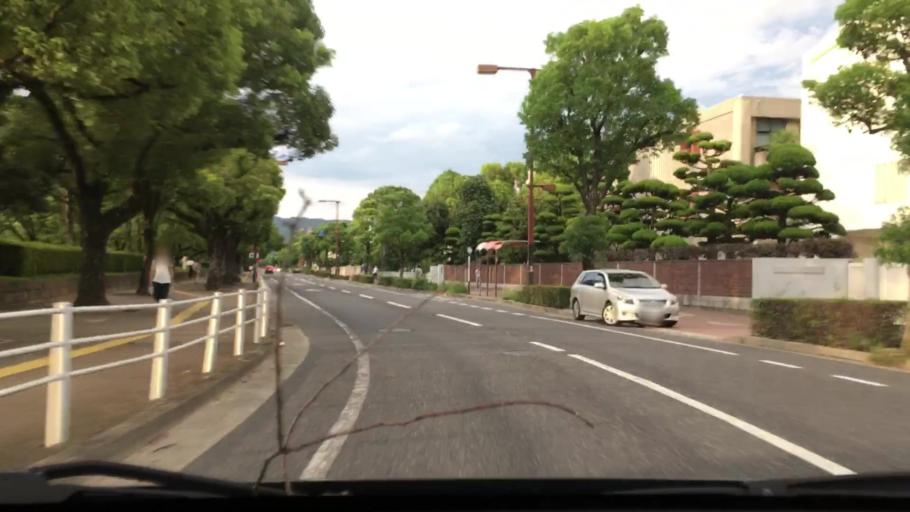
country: JP
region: Hyogo
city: Himeji
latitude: 34.8359
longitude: 134.6964
